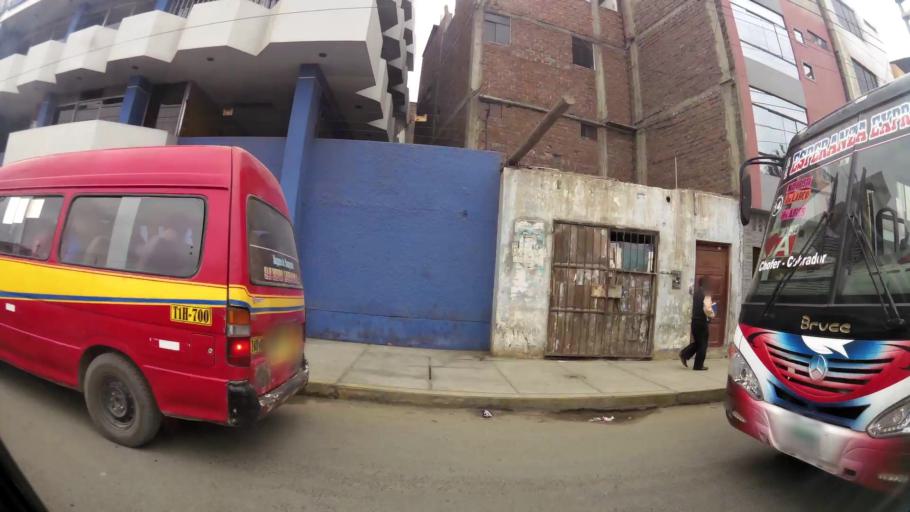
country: PE
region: La Libertad
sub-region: Provincia de Trujillo
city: Trujillo
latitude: -8.1145
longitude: -79.0214
